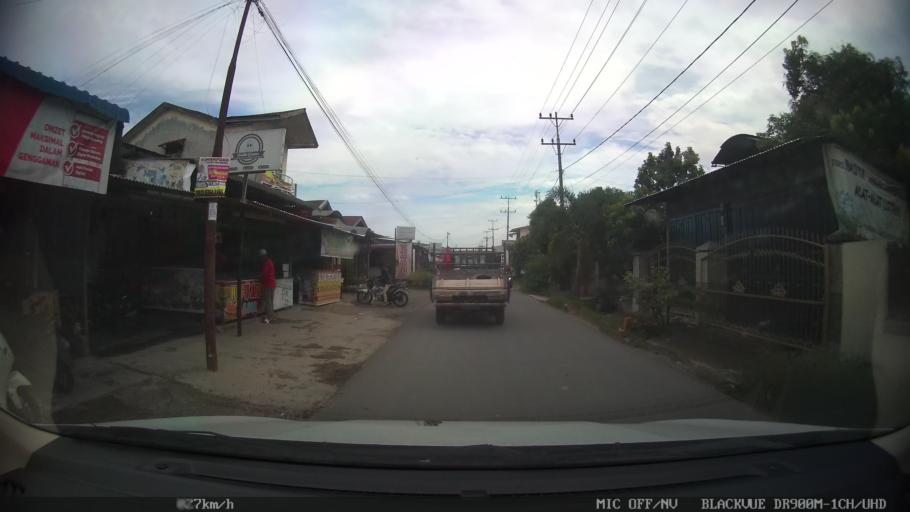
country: ID
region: North Sumatra
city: Sunggal
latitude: 3.6068
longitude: 98.5802
